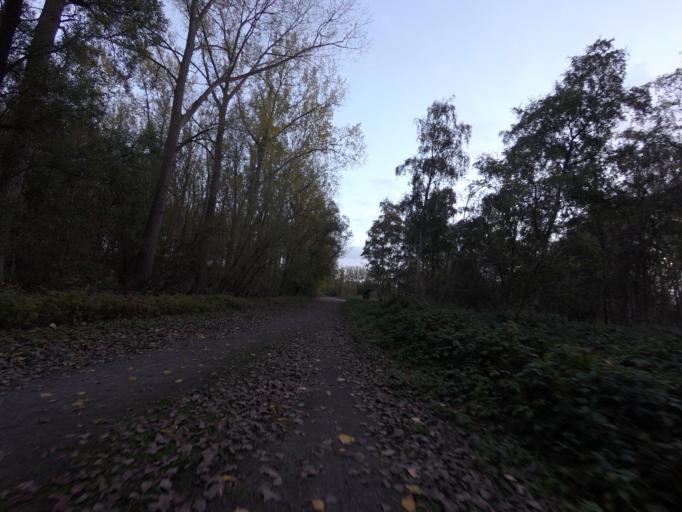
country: BE
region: Flanders
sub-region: Provincie Antwerpen
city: Zwijndrecht
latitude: 51.2307
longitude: 4.3631
